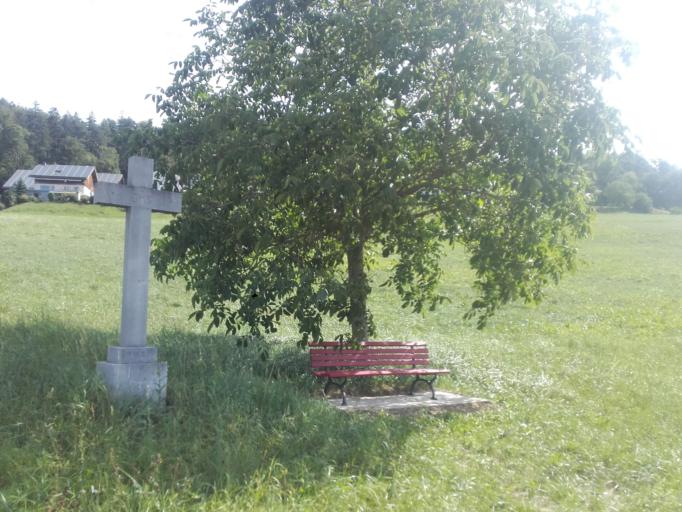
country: CH
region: Solothurn
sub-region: Bezirk Thal
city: Laupersdorf
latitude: 47.3178
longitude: 7.6565
